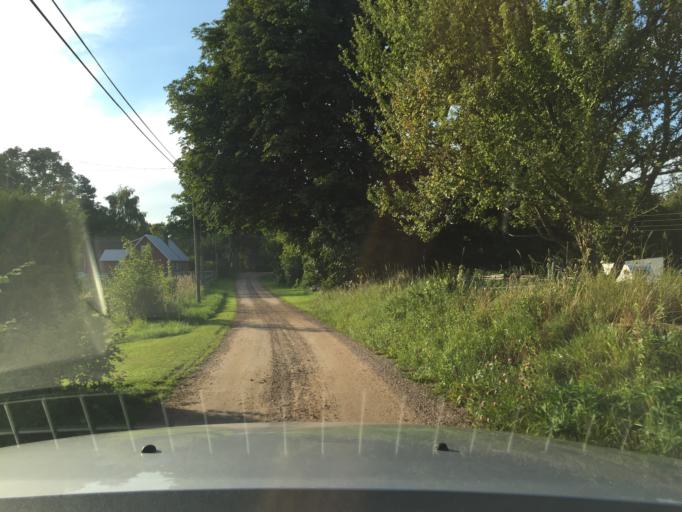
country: SE
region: Skane
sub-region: Hassleholms Kommun
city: Sosdala
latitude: 56.0228
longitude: 13.6944
